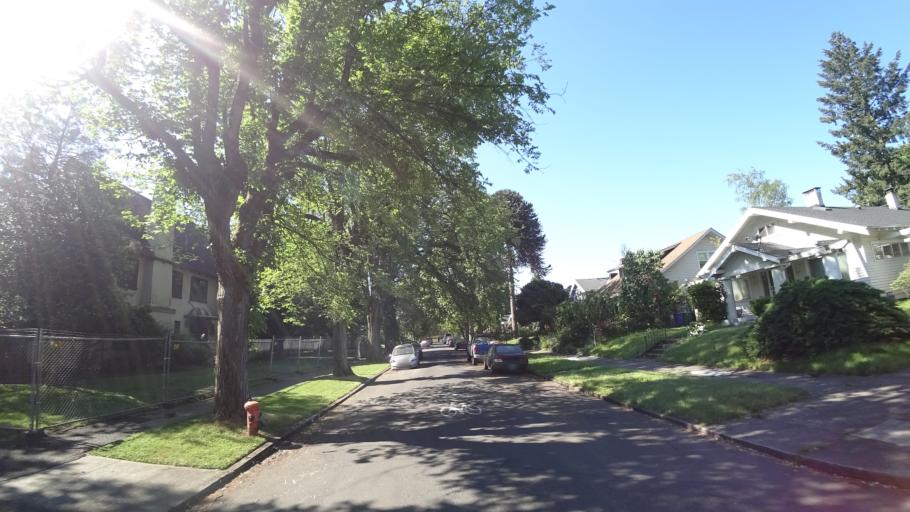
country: US
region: Oregon
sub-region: Multnomah County
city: Portland
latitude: 45.5604
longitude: -122.6648
